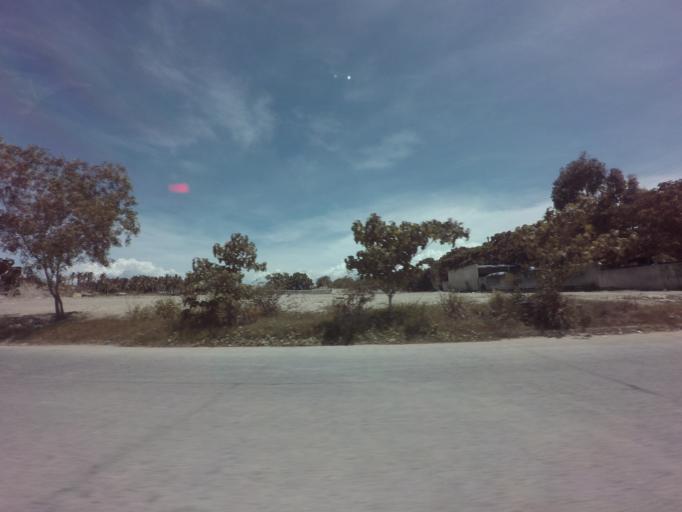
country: PH
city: Sambayanihan People's Village
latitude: 14.5061
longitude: 120.9871
